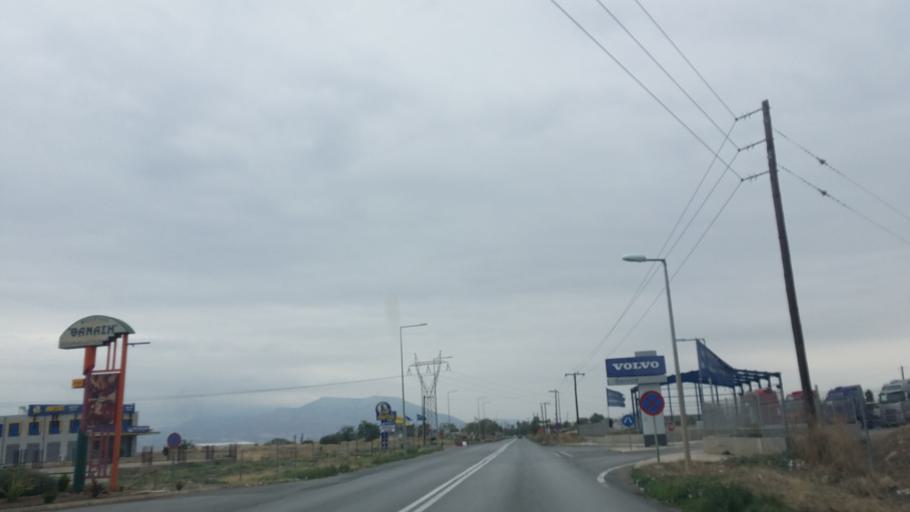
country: GR
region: Central Greece
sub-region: Nomos Voiotias
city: Thivai
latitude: 38.3345
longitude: 23.3127
